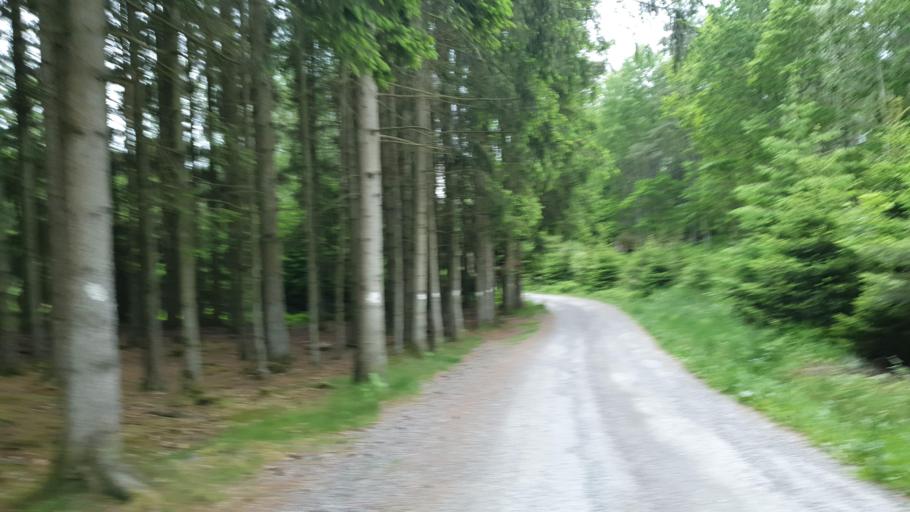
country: SE
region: Vaestra Goetaland
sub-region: Molndal
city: Kallered
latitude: 57.6167
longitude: 12.0579
